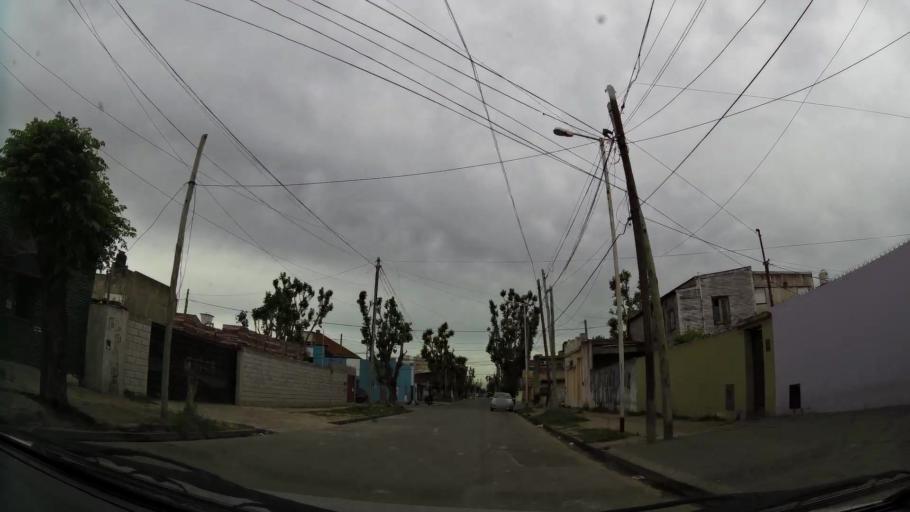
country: AR
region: Buenos Aires
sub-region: Partido de Avellaneda
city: Avellaneda
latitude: -34.6549
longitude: -58.3557
